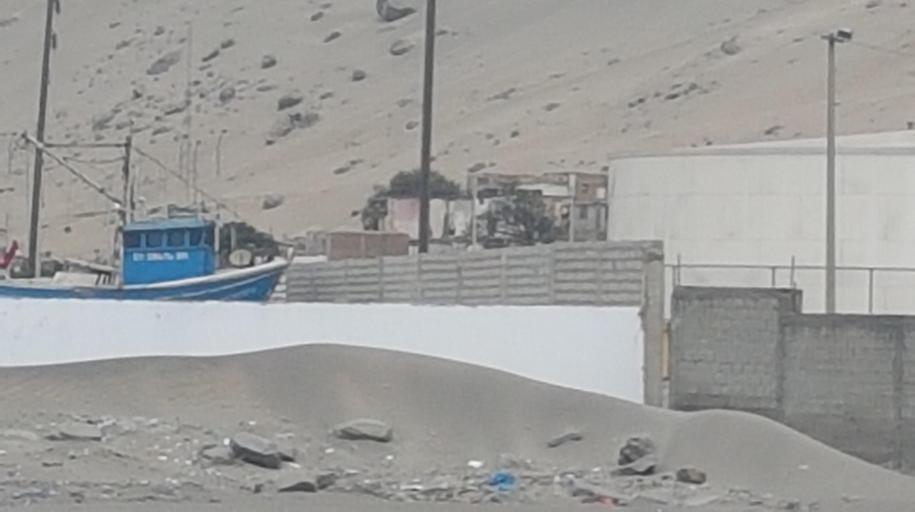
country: PE
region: La Libertad
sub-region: Provincia de Trujillo
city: Salaverry
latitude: -8.2236
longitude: -78.9817
